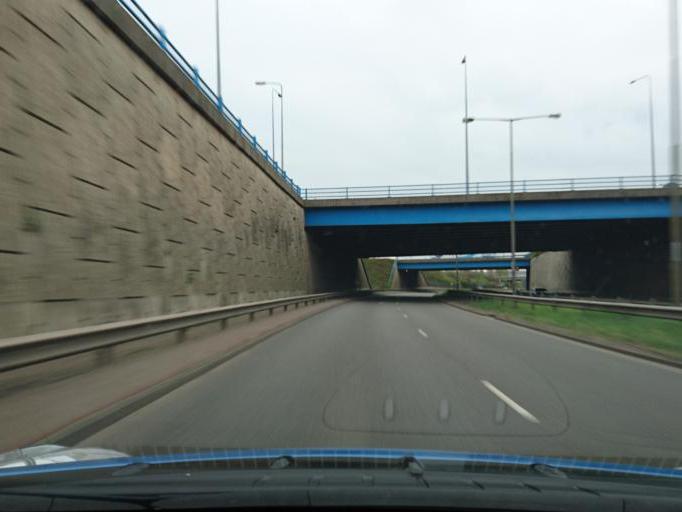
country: GB
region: England
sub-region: Stoke-on-Trent
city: Stoke-on-Trent
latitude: 52.9916
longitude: -2.1827
